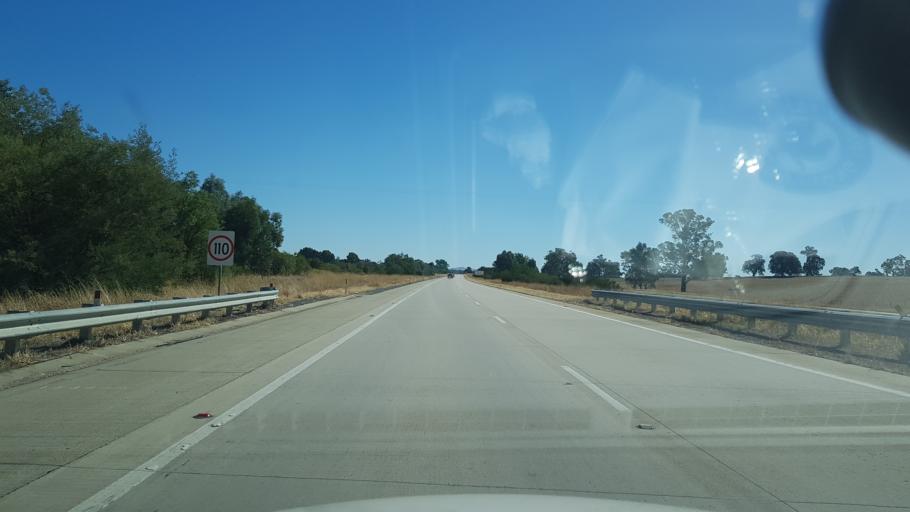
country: AU
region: New South Wales
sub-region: Greater Hume Shire
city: Jindera
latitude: -35.9252
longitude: 147.0312
